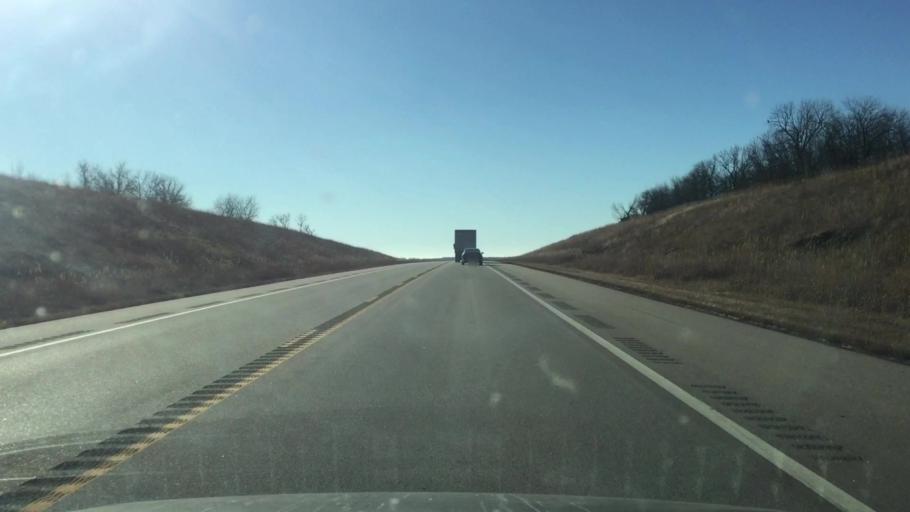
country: US
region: Kansas
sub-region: Allen County
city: Iola
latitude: 38.0131
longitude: -95.3808
